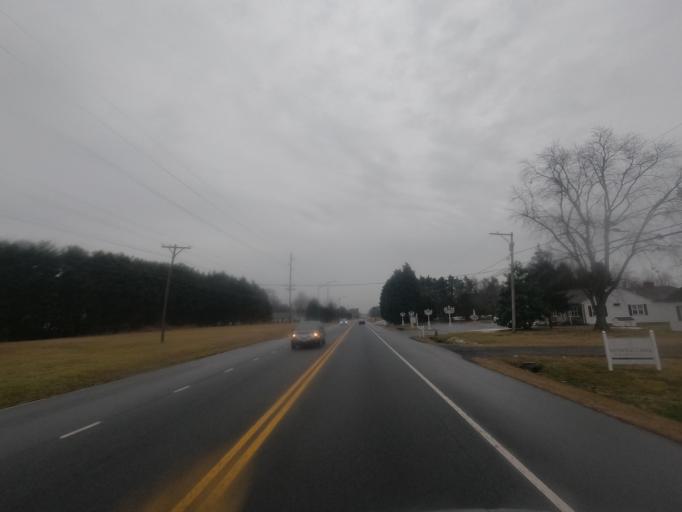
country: US
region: Maryland
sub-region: Dorchester County
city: Cambridge
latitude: 38.5724
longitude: -75.9820
